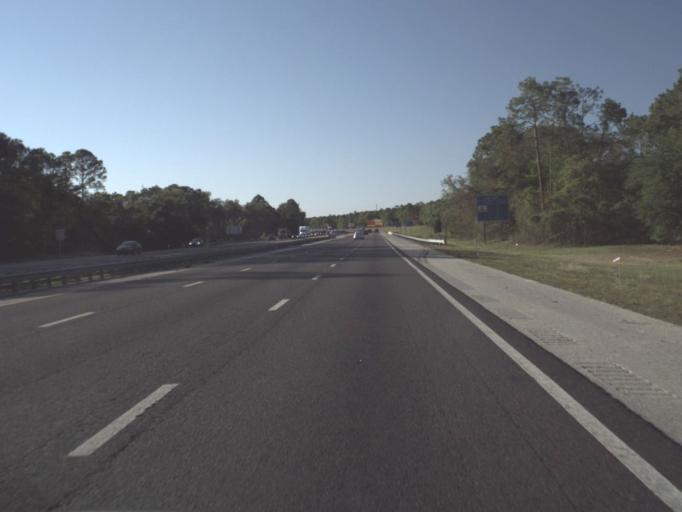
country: US
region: Florida
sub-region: Flagler County
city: Palm Coast
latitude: 29.6499
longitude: -81.2750
